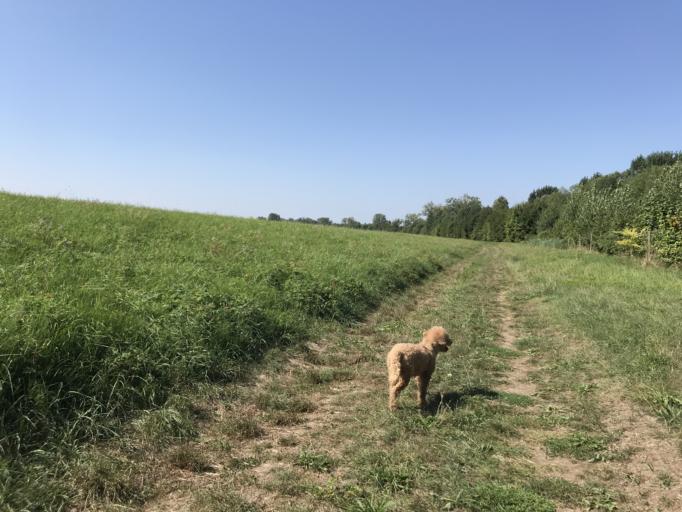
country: DE
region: Hesse
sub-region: Regierungsbezirk Darmstadt
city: Bischofsheim
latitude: 50.0009
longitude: 8.3719
